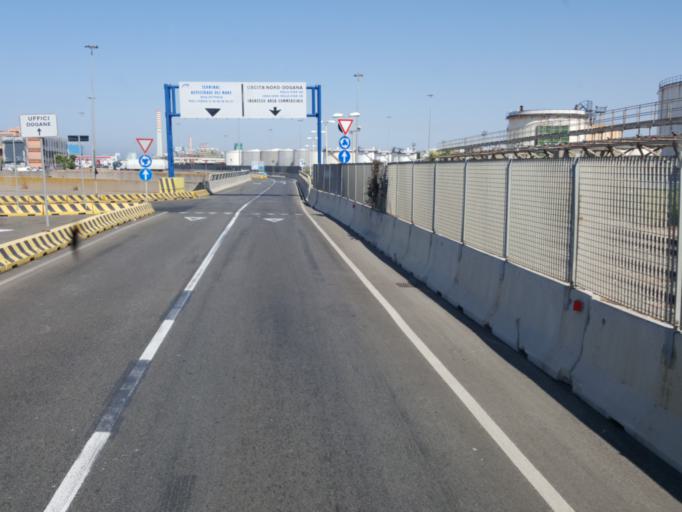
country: IT
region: Latium
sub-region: Citta metropolitana di Roma Capitale
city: Civitavecchia
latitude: 42.1025
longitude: 11.7823
